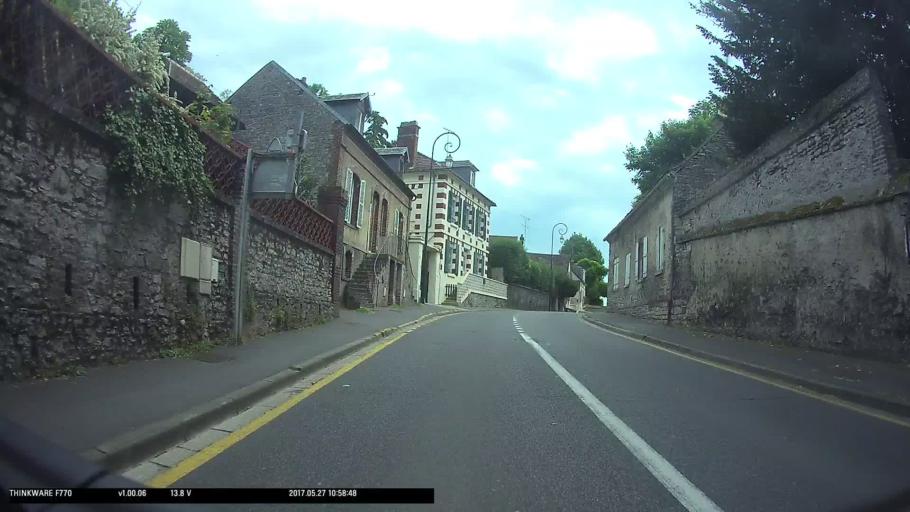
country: FR
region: Picardie
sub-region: Departement de l'Oise
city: Chaumont-en-Vexin
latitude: 49.2624
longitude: 1.8781
